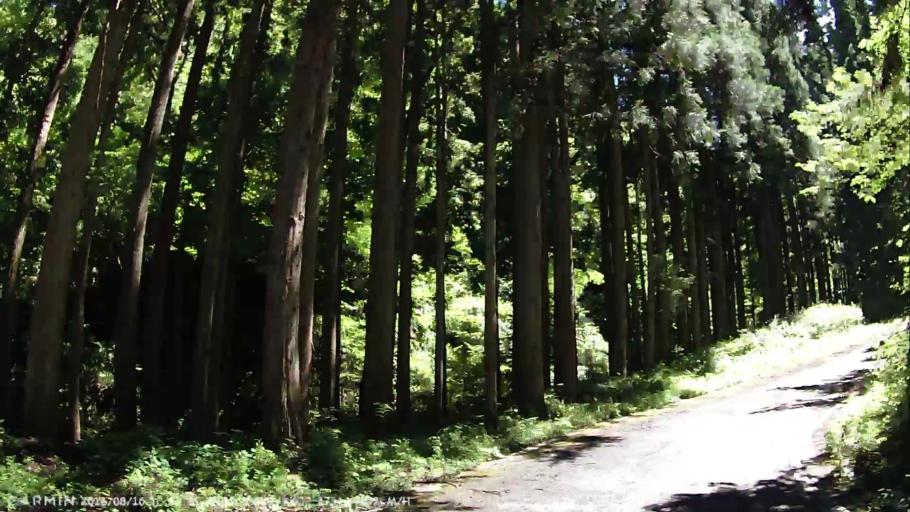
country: JP
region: Fukushima
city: Kitakata
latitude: 37.3731
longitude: 139.8564
